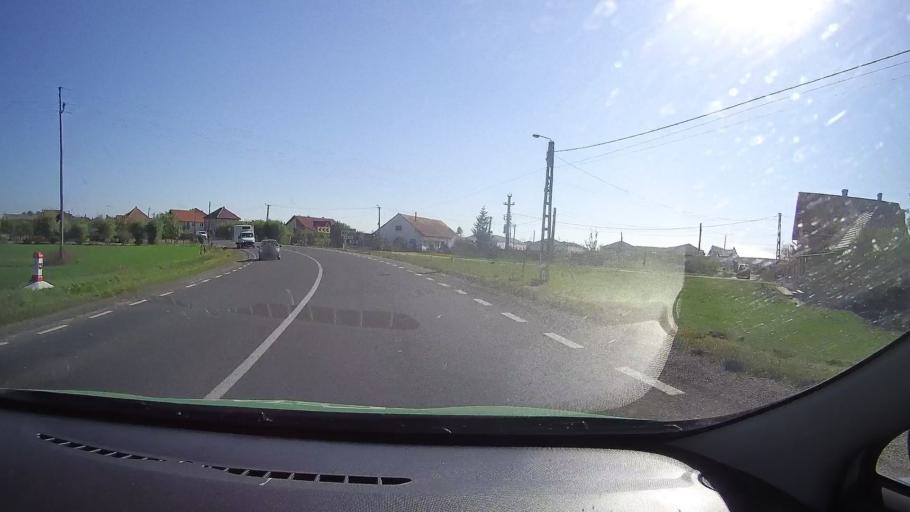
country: RO
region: Satu Mare
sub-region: Oras Ardud
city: Ardud
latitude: 47.6541
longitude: 22.8862
